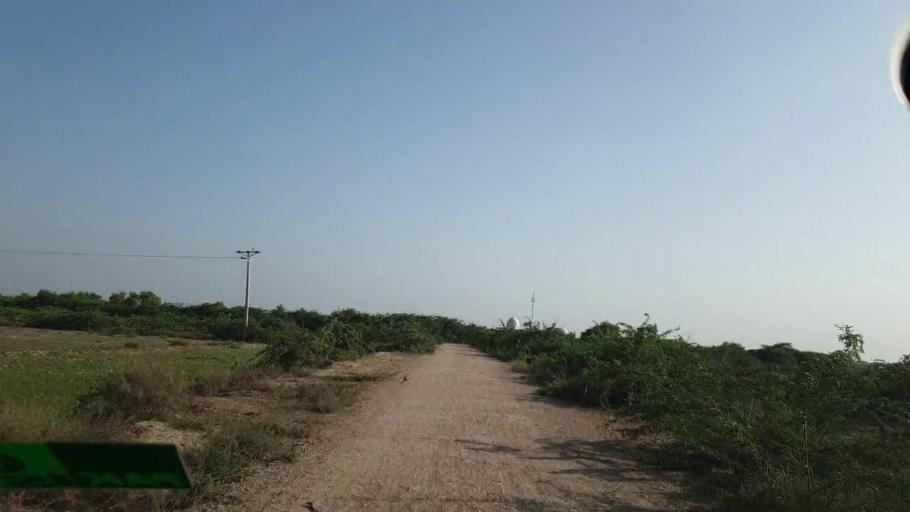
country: PK
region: Sindh
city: Naukot
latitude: 24.7374
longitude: 69.2477
